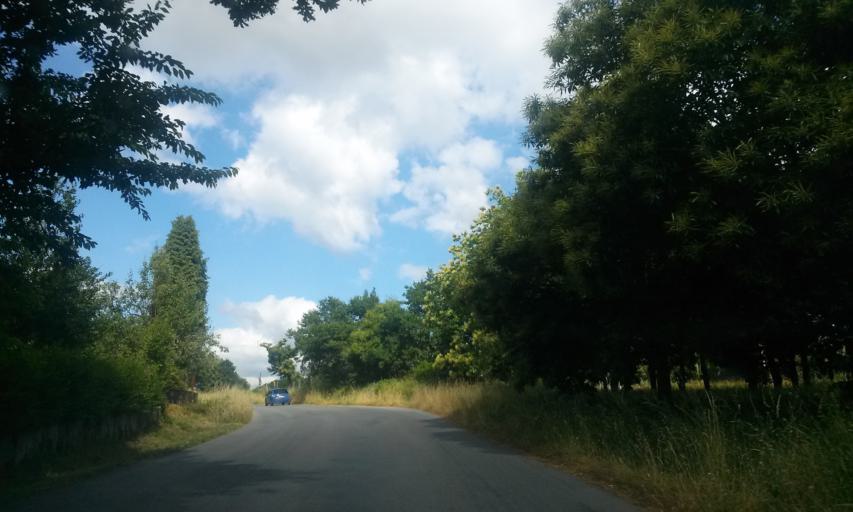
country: ES
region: Galicia
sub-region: Provincia de Lugo
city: Rabade
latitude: 43.1154
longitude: -7.6532
